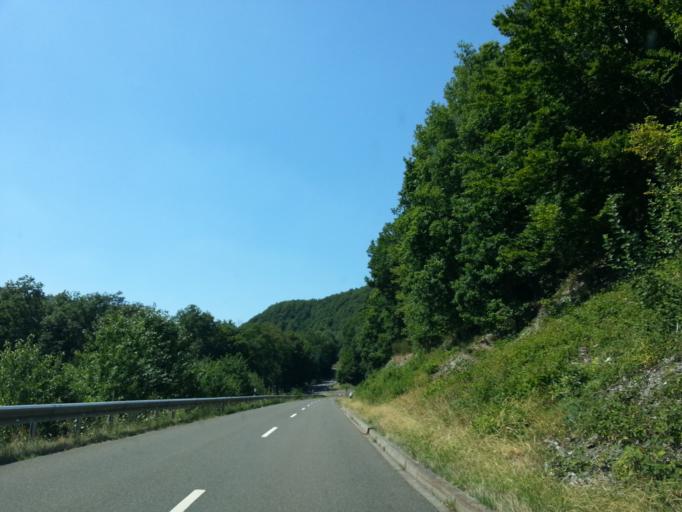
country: DE
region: Rheinland-Pfalz
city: Piesport
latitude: 49.8911
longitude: 6.9118
